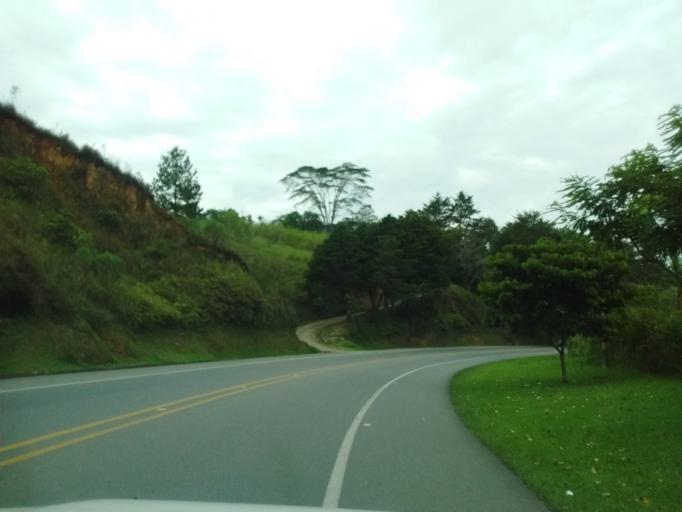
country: CO
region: Cauca
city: Cajibio
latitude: 2.5498
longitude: -76.5658
